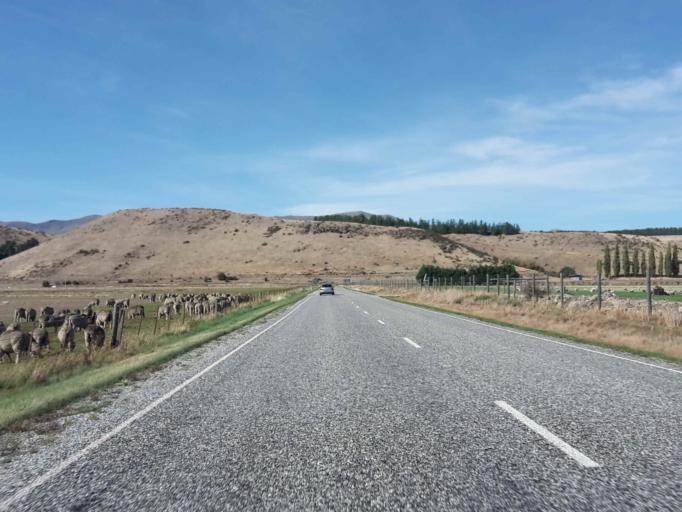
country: NZ
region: Otago
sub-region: Queenstown-Lakes District
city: Wanaka
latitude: -44.8391
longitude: 169.3921
